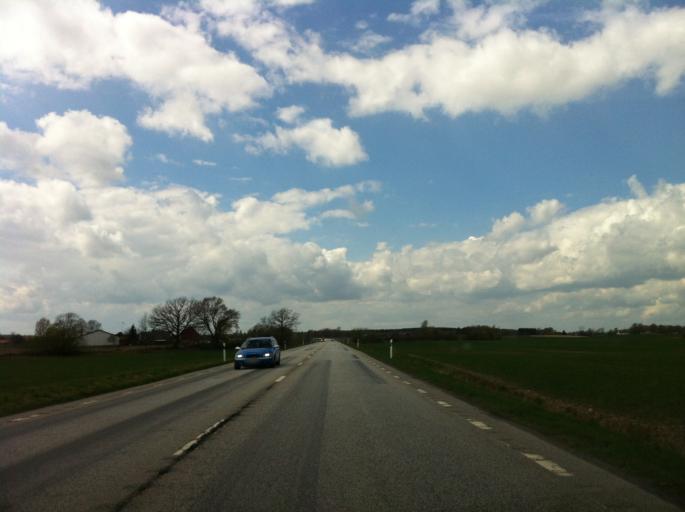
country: SE
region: Skane
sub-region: Eslovs Kommun
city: Stehag
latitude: 55.8484
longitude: 13.4317
